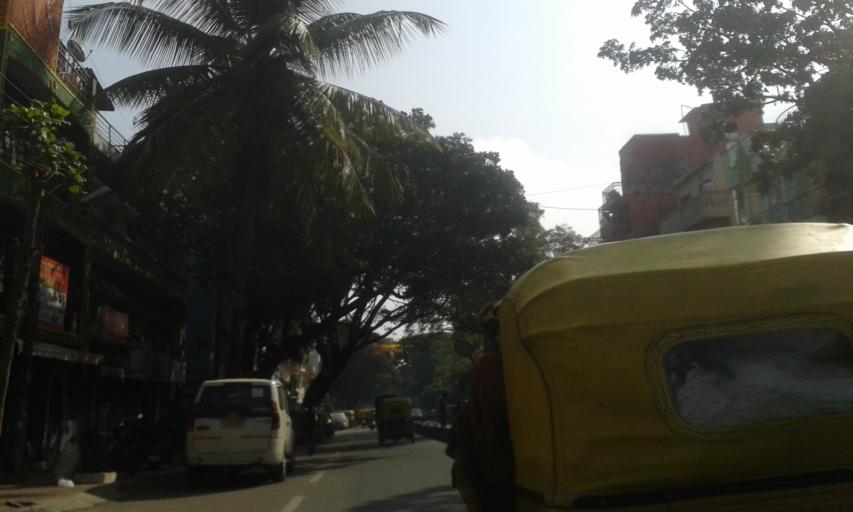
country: IN
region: Karnataka
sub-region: Bangalore Urban
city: Bangalore
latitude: 12.9286
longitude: 77.5939
